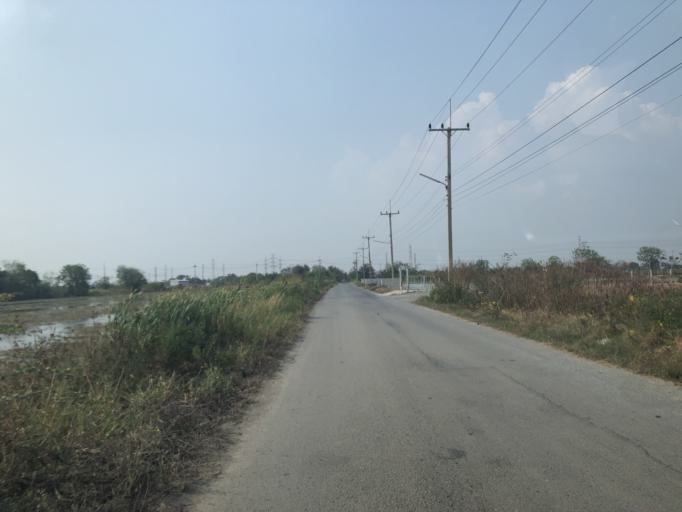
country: TH
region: Chachoengsao
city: Bang Pakong
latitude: 13.5146
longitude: 100.9403
